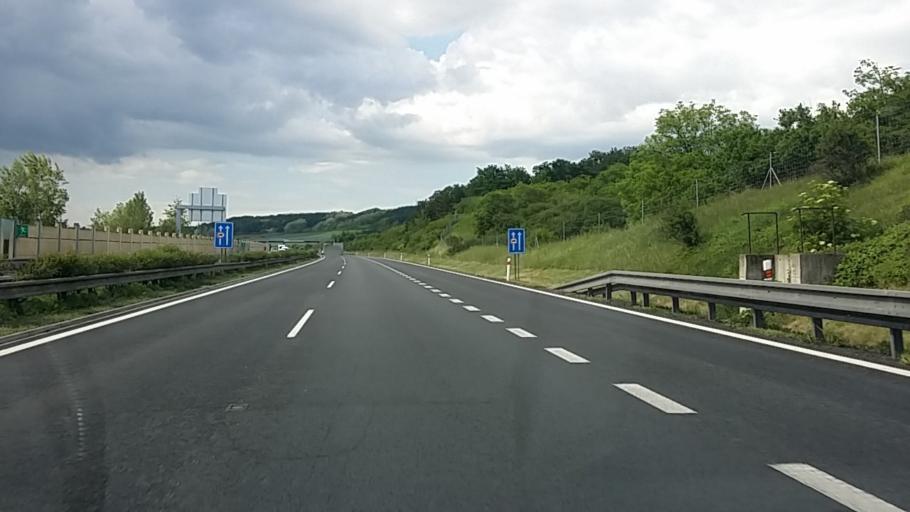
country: CZ
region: Central Bohemia
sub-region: Okres Melnik
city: Veltrusy
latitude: 50.3145
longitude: 14.3133
